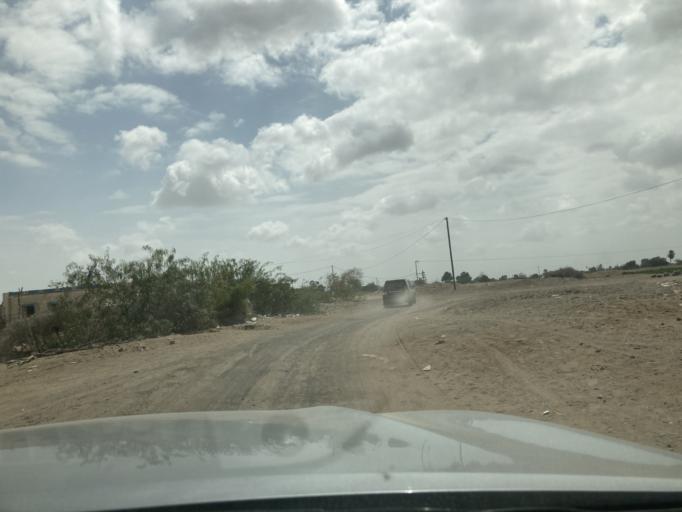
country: YE
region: Lahij
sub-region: Al  Hawtah
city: Lahij
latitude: 13.0189
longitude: 45.0029
